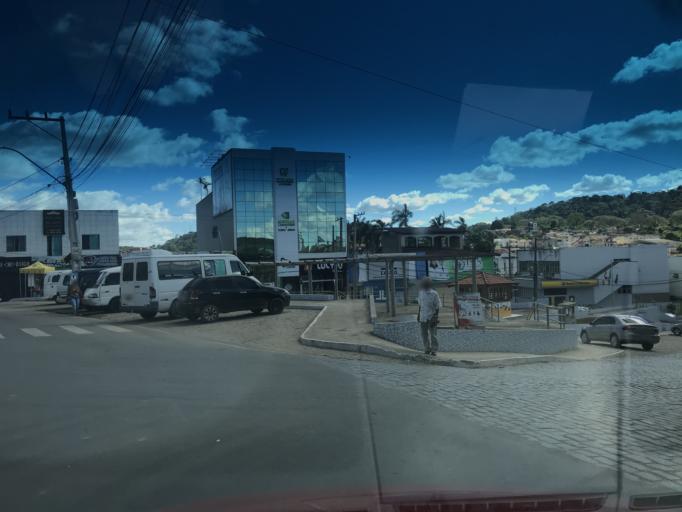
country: BR
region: Bahia
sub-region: Gandu
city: Gandu
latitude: -13.7458
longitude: -39.4874
